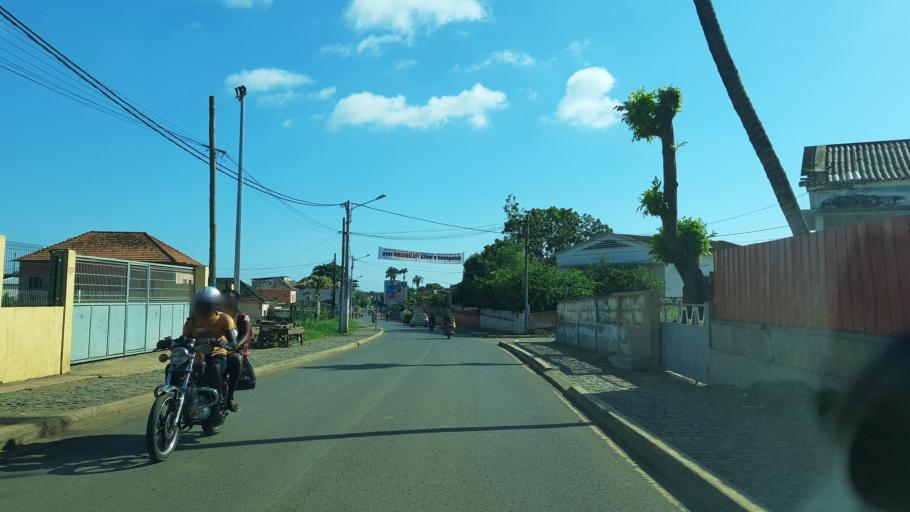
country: ST
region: Sao Tome Island
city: Sao Tome
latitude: 0.3320
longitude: 6.7304
